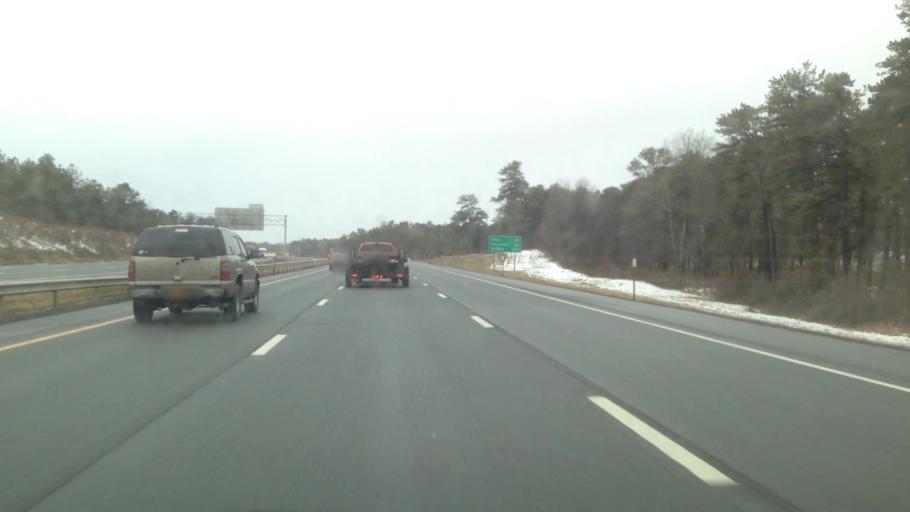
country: US
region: New York
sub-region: Albany County
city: Westmere
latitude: 42.7161
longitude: -73.8715
